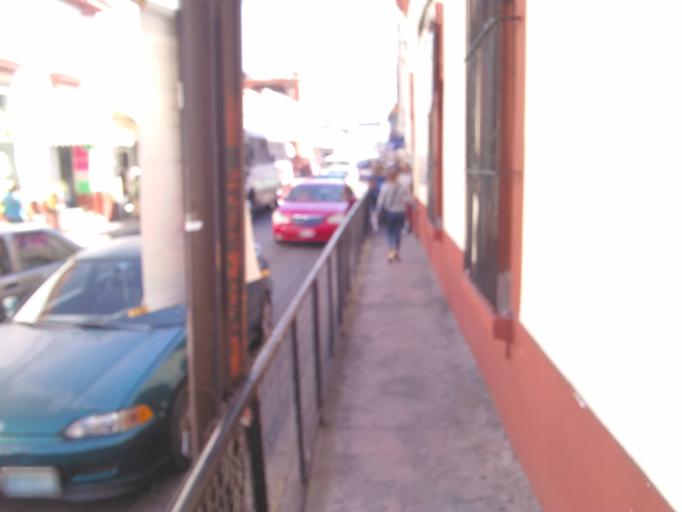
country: MX
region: Nayarit
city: Tepic
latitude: 21.5096
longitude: -104.8933
